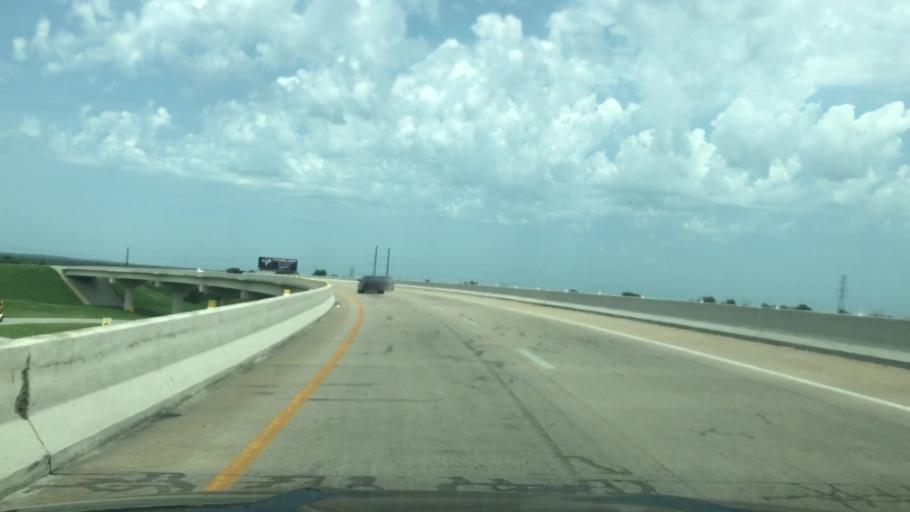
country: US
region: Oklahoma
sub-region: Rogers County
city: Catoosa
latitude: 36.1629
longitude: -95.7322
